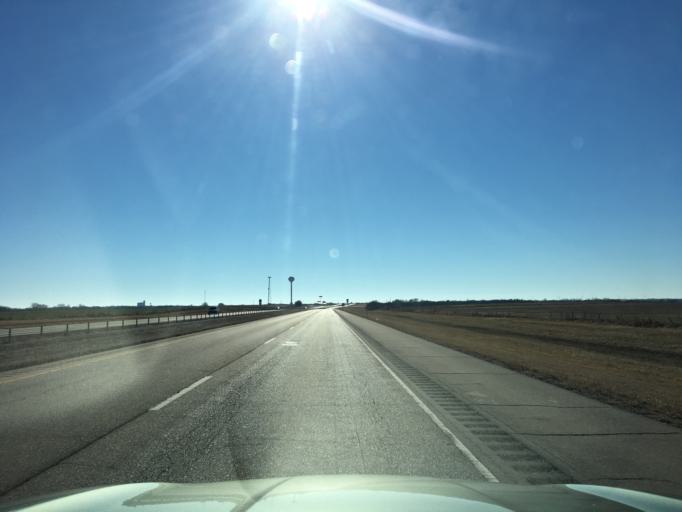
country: US
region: Oklahoma
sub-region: Kay County
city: Blackwell
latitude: 36.9525
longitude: -97.3458
